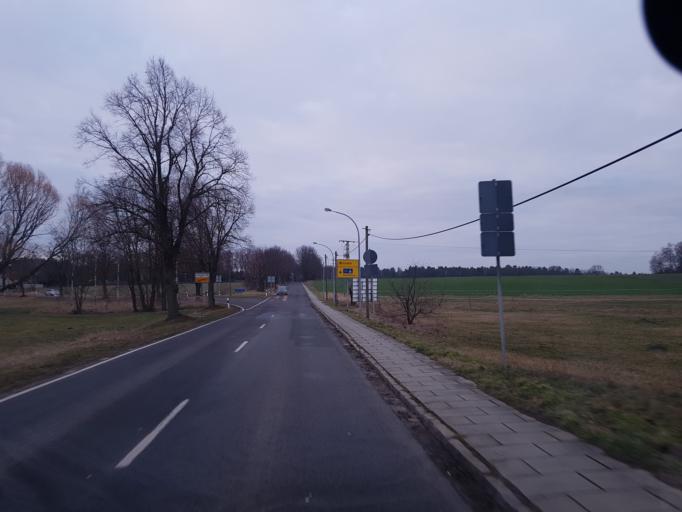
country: DE
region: Brandenburg
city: Schipkau
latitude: 51.5400
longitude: 13.8964
